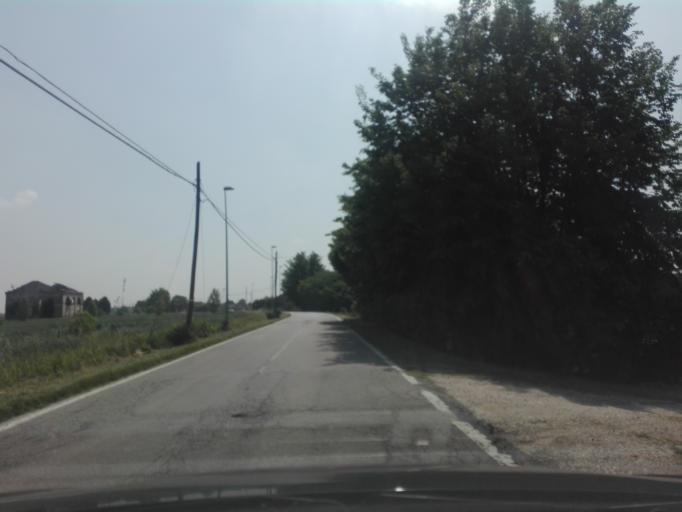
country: IT
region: Veneto
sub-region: Provincia di Rovigo
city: Ceregnano
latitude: 45.0460
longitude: 11.8842
